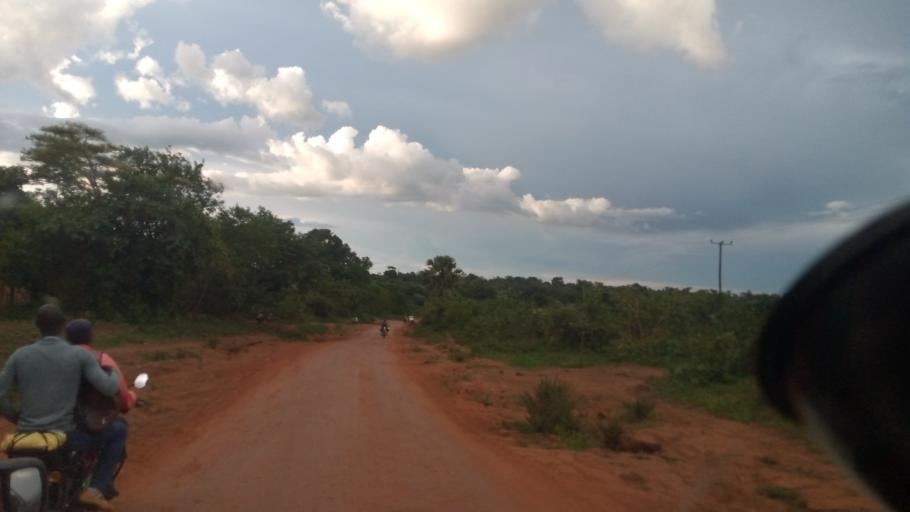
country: UG
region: Northern Region
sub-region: Kole District
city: Kole
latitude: 2.3823
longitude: 32.9326
